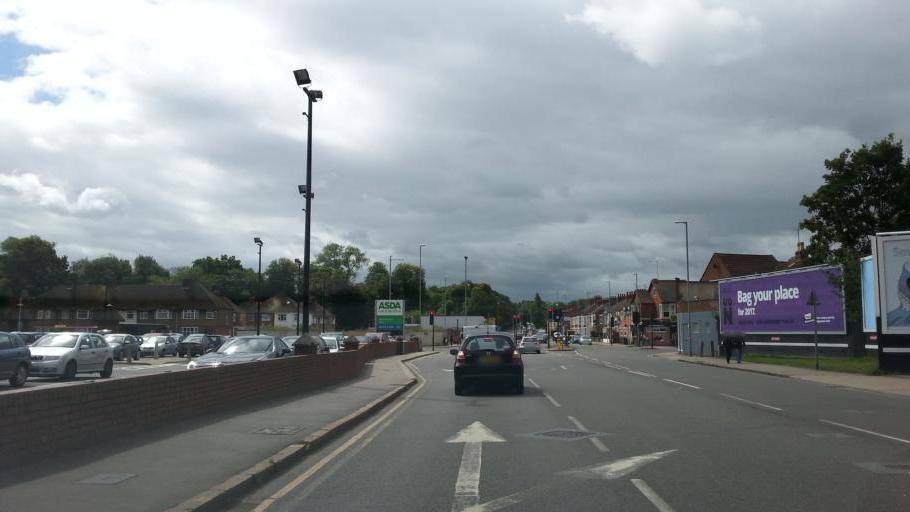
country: GB
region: England
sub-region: Northamptonshire
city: Hardingstone
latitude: 52.2289
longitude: -0.8964
